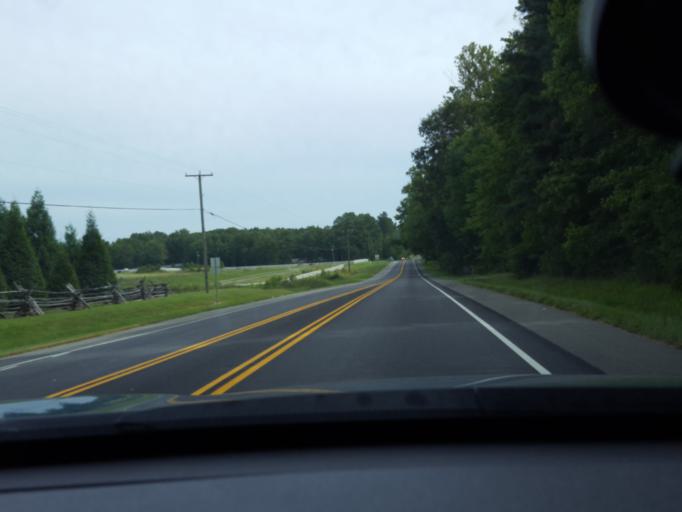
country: US
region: Virginia
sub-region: Hanover County
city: Hanover
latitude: 37.7503
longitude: -77.3603
